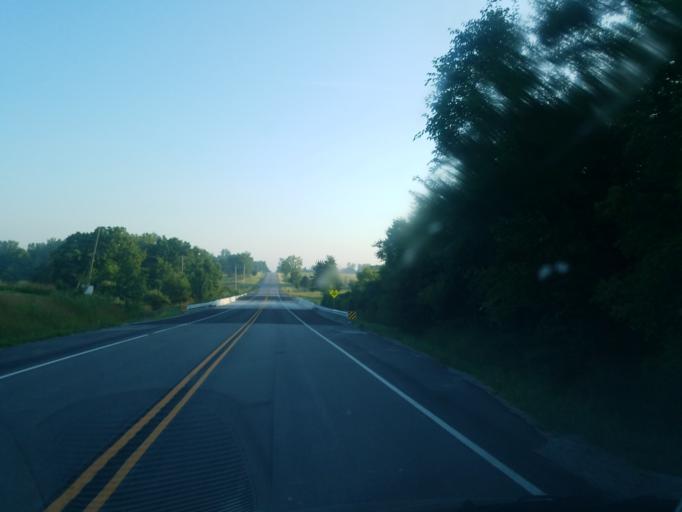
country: US
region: Indiana
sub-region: Allen County
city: Harlan
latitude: 41.2526
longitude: -84.8662
